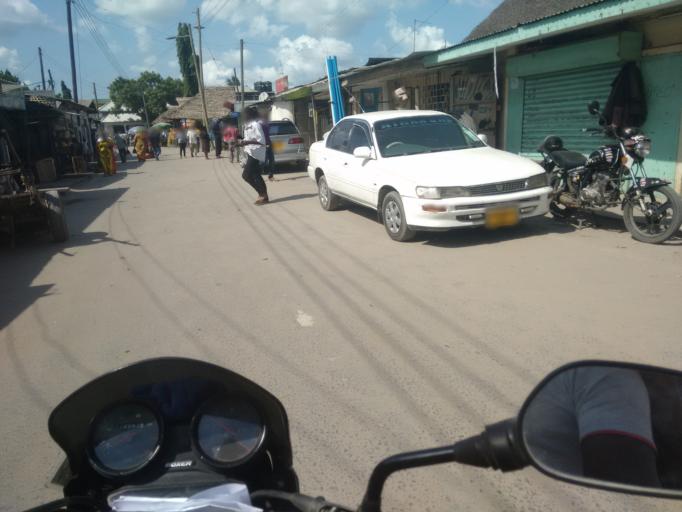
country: TZ
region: Dar es Salaam
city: Dar es Salaam
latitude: -6.8400
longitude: 39.2730
